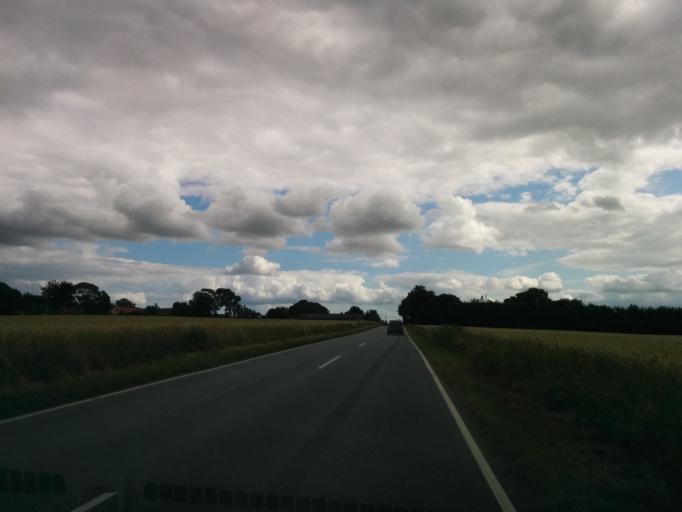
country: DK
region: Central Jutland
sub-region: Arhus Kommune
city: Kolt
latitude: 56.1149
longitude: 10.0696
